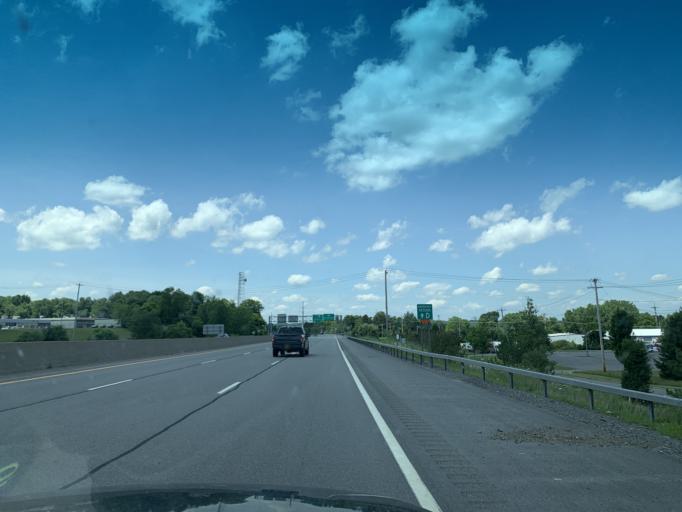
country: US
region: New York
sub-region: Oneida County
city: New Hartford
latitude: 43.0826
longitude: -75.2950
